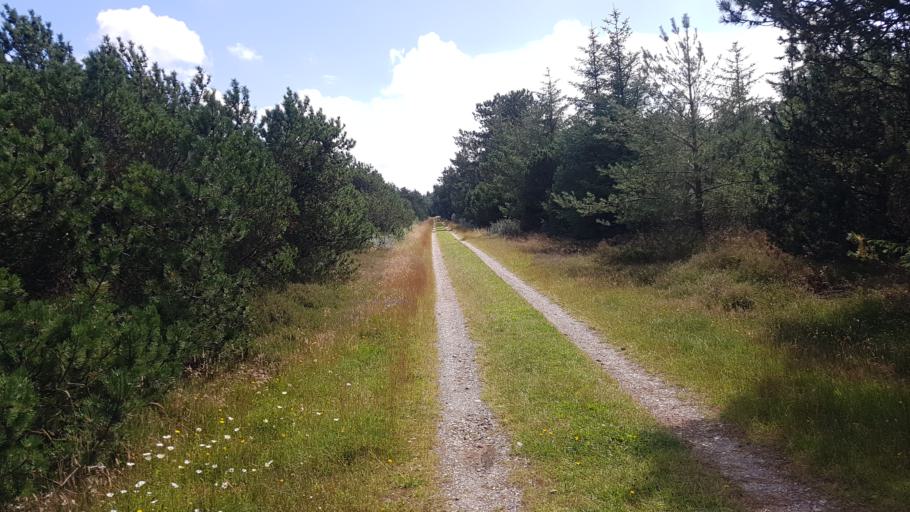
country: DE
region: Schleswig-Holstein
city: List
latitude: 55.1212
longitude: 8.5386
